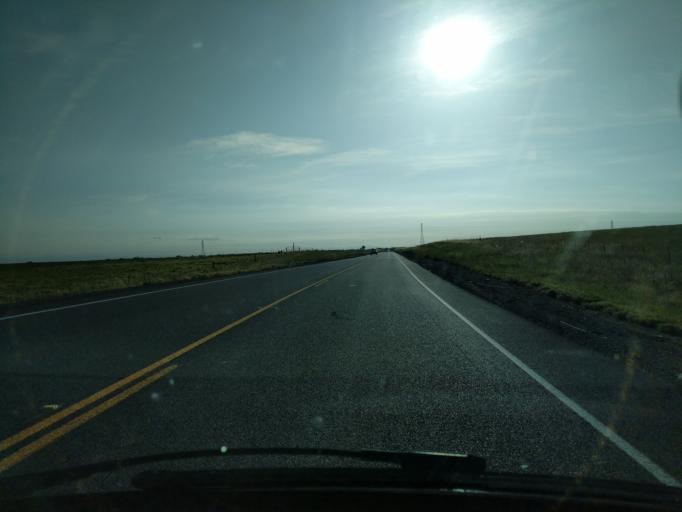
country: US
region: California
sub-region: San Joaquin County
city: Escalon
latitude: 37.9304
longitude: -120.9496
